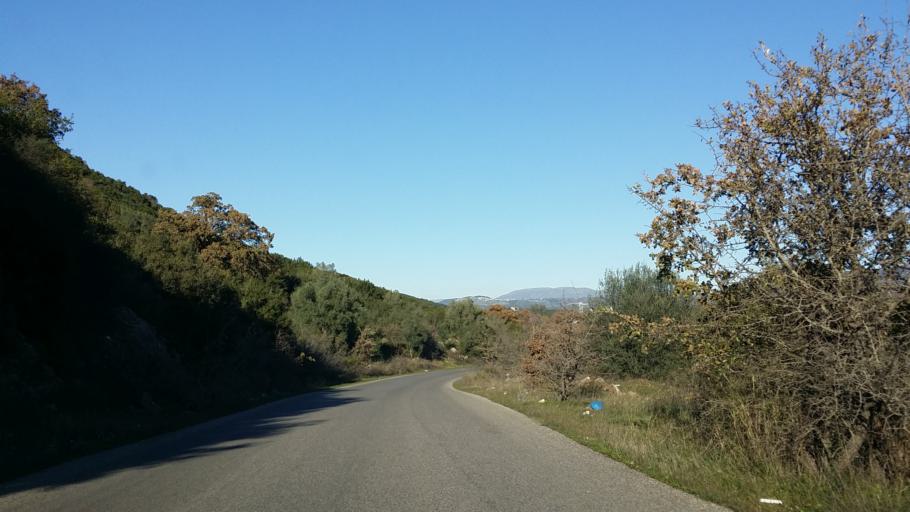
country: GR
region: West Greece
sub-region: Nomos Aitolias kai Akarnanias
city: Fitiai
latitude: 38.6145
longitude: 21.1411
